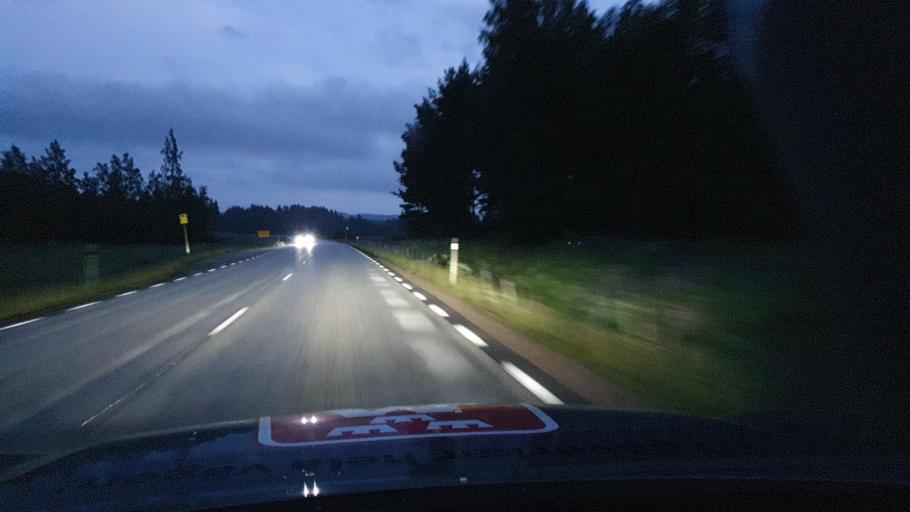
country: SE
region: Vaermland
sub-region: Storfors Kommun
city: Storfors
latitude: 59.5116
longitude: 14.3038
